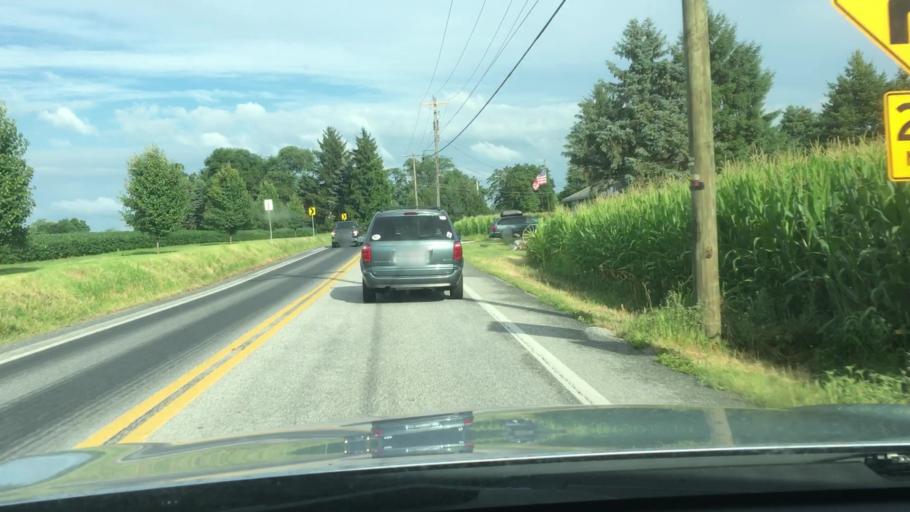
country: US
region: Pennsylvania
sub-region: York County
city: Dillsburg
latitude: 40.1478
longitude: -77.0660
